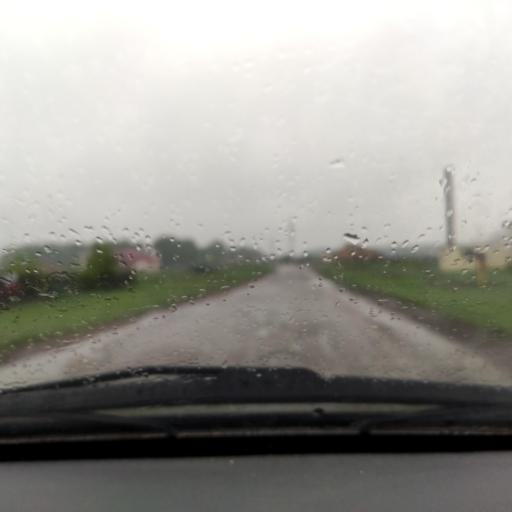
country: RU
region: Bashkortostan
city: Asanovo
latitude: 54.7630
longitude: 55.4907
